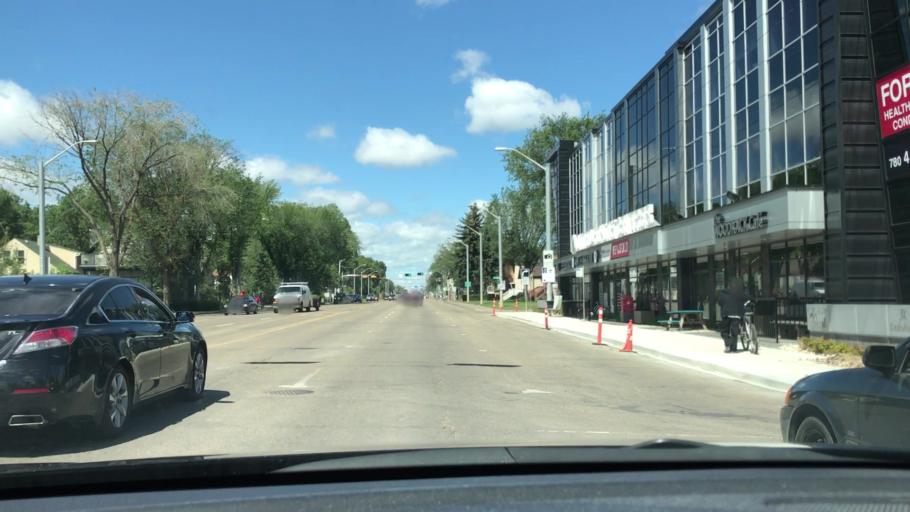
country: CA
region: Alberta
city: Edmonton
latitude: 53.5123
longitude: -113.5119
